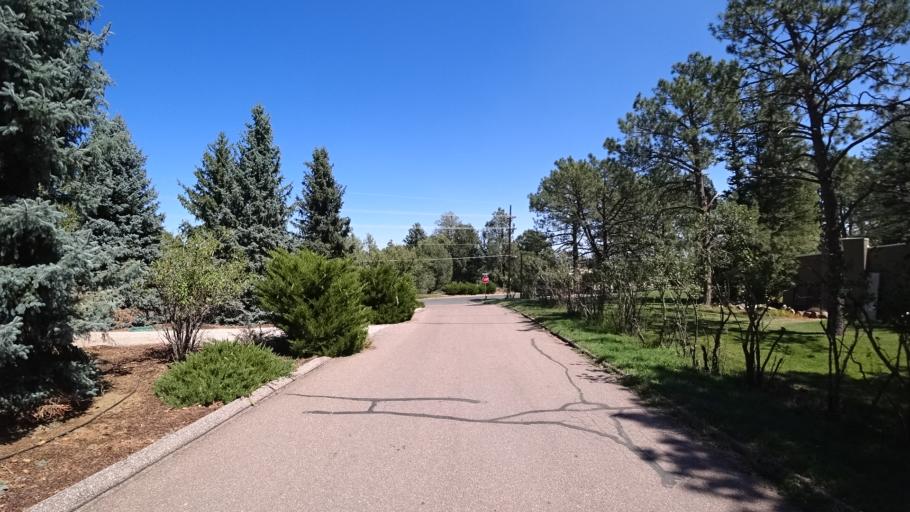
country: US
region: Colorado
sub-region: El Paso County
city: Colorado Springs
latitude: 38.7810
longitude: -104.8414
